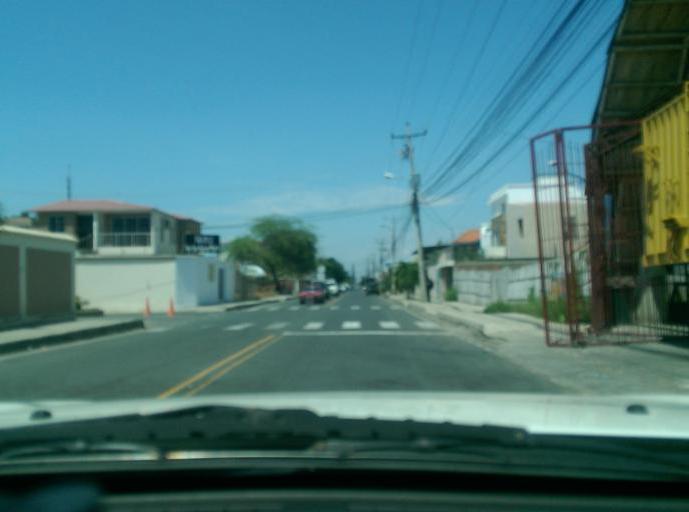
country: EC
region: Manabi
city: Manta
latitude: -0.9573
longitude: -80.7544
